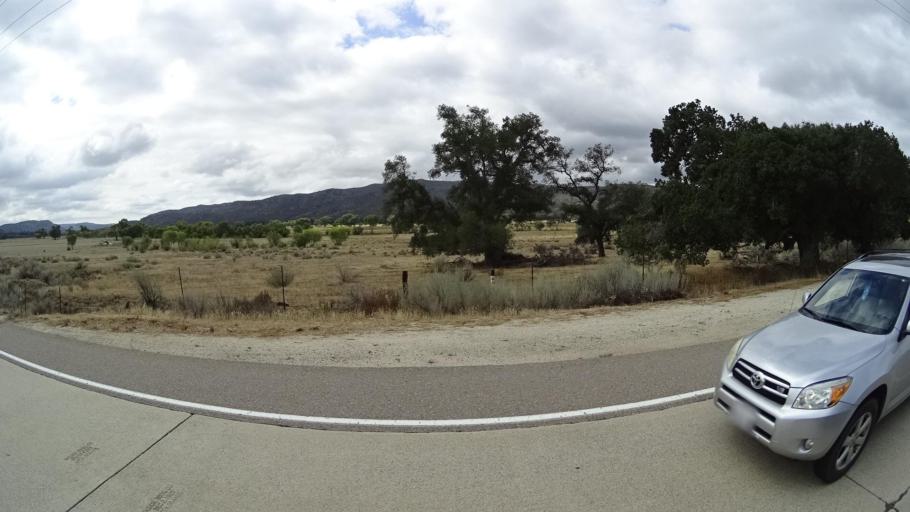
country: US
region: California
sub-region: San Diego County
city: Pine Valley
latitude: 32.7471
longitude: -116.4828
